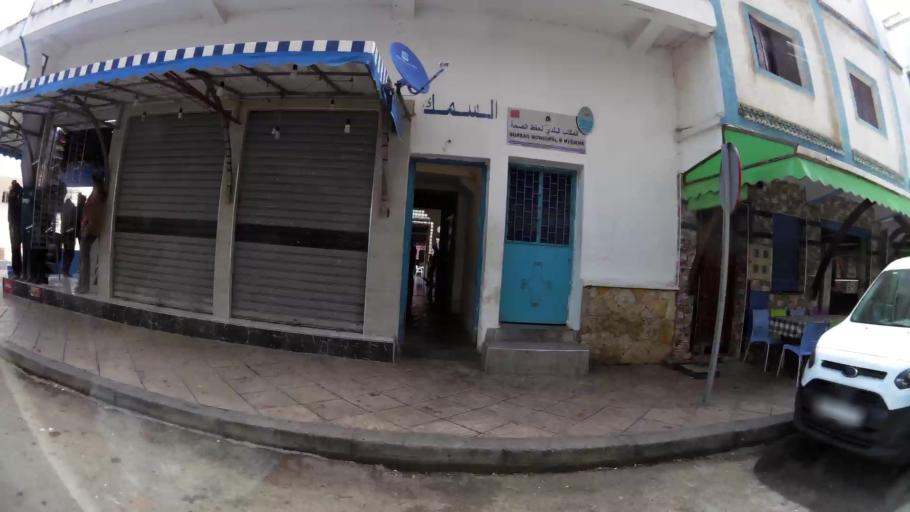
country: MA
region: Tanger-Tetouan
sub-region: Tetouan
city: Martil
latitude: 35.6840
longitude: -5.3227
